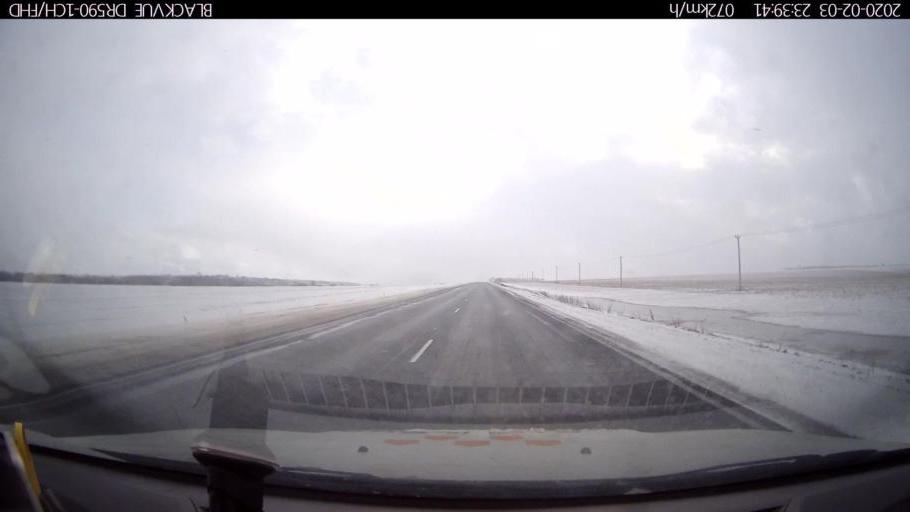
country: RU
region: Nizjnij Novgorod
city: Dal'neye Konstantinovo
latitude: 55.8813
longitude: 44.1374
